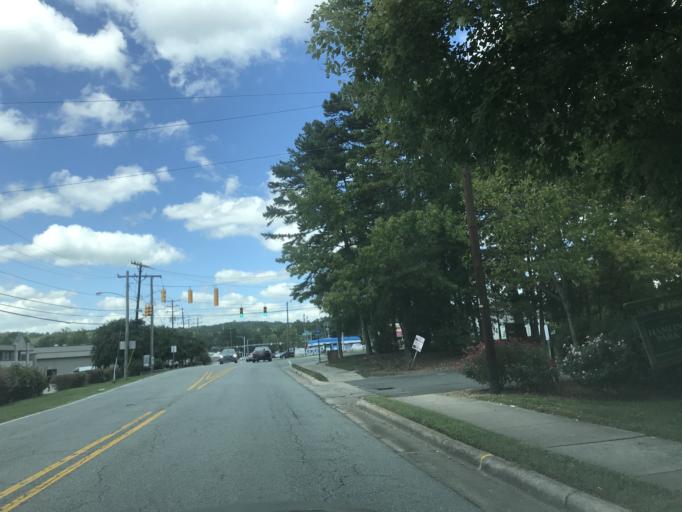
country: US
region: North Carolina
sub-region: Orange County
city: Chapel Hill
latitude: 35.9347
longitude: -79.0215
